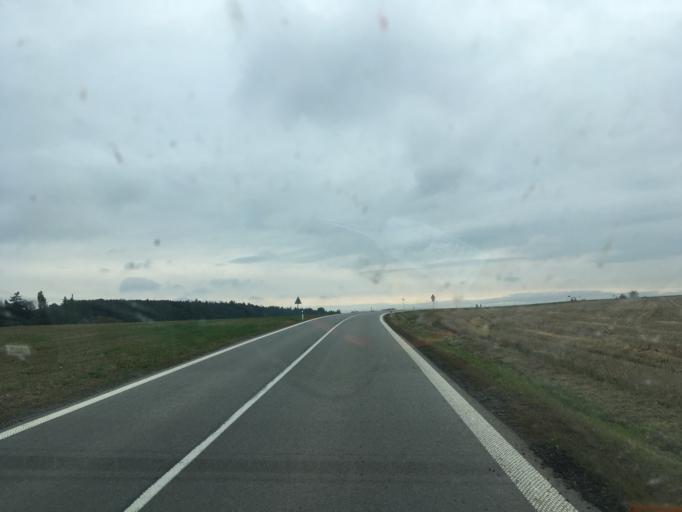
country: CZ
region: South Moravian
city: Zbraslav
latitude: 49.1950
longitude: 16.2324
